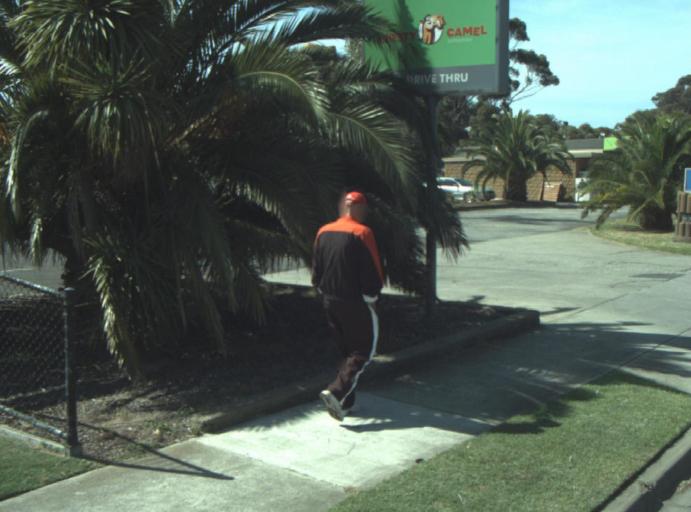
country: AU
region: Victoria
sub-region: Greater Geelong
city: Hamlyn Heights
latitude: -38.1253
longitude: 144.3406
